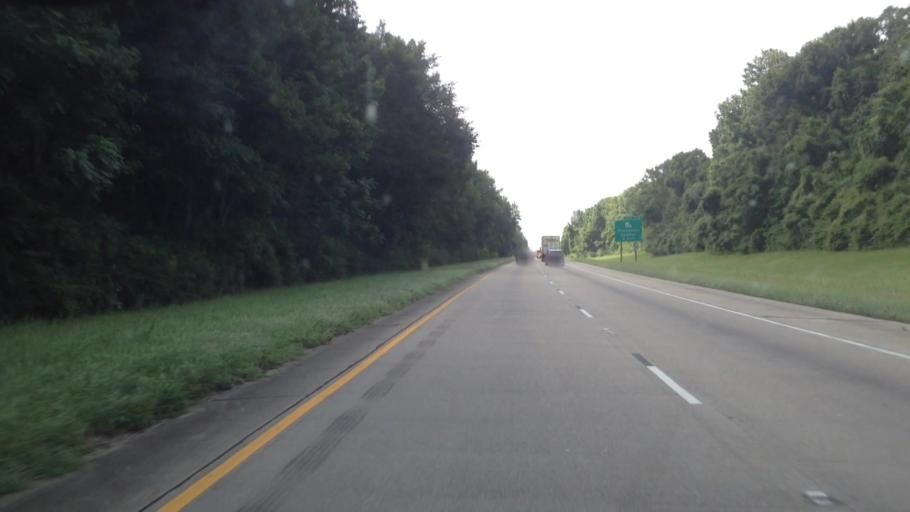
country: US
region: Louisiana
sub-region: Ascension Parish
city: Prairieville
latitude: 30.3028
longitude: -90.9933
